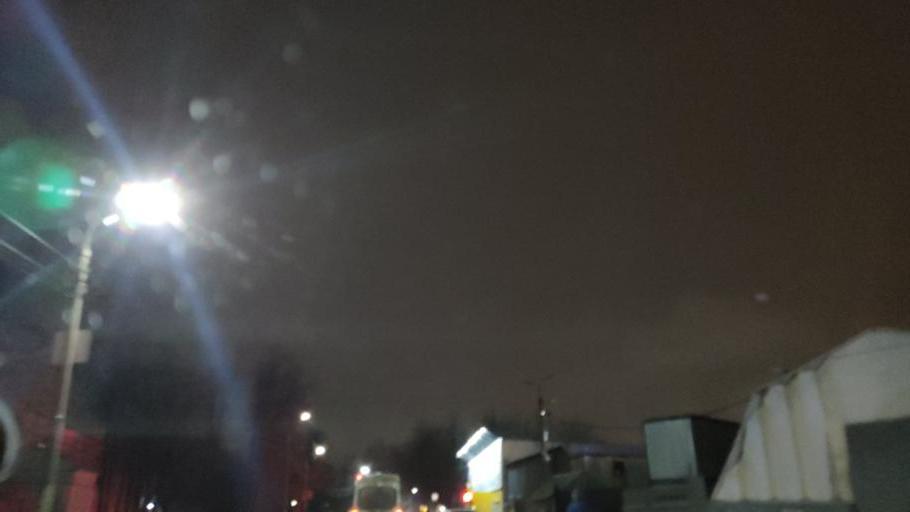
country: RU
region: Moskovskaya
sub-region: Podol'skiy Rayon
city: Podol'sk
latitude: 55.4357
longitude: 37.5720
